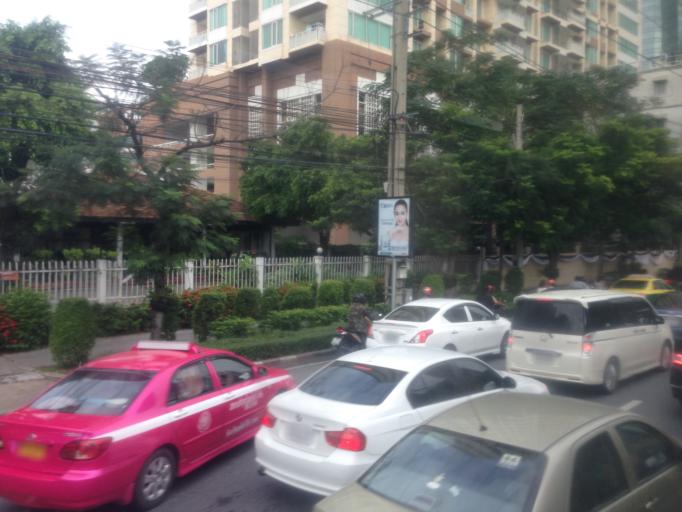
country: TH
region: Bangkok
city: Sathon
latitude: 13.7186
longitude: 100.5317
